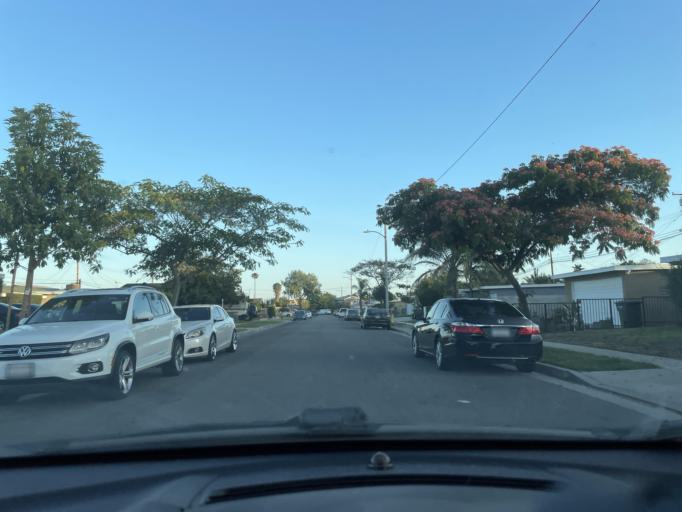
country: US
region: California
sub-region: Los Angeles County
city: La Mirada
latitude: 33.9123
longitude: -118.0323
